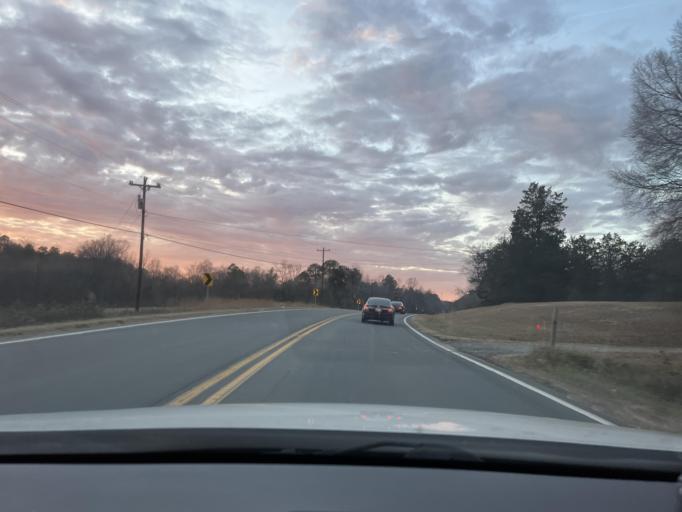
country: US
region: North Carolina
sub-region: Guilford County
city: McLeansville
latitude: 36.0799
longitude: -79.6429
